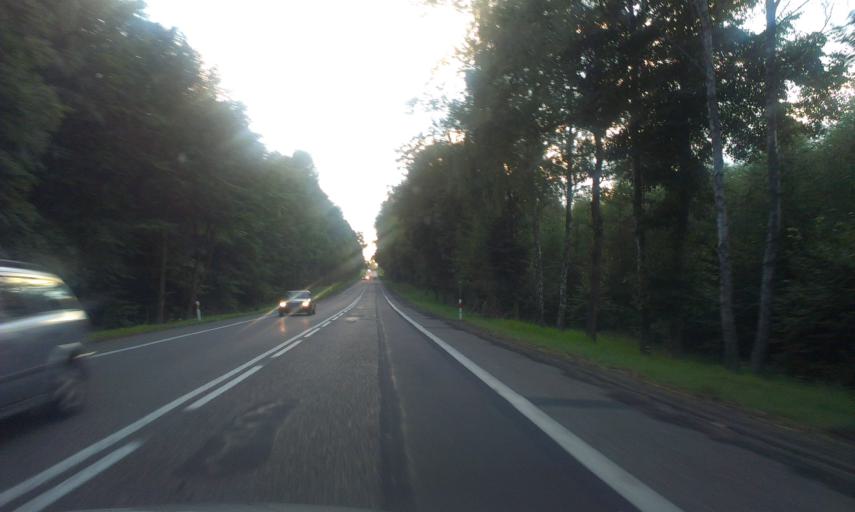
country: PL
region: West Pomeranian Voivodeship
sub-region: Powiat koszalinski
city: Sianow
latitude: 54.2558
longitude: 16.3750
